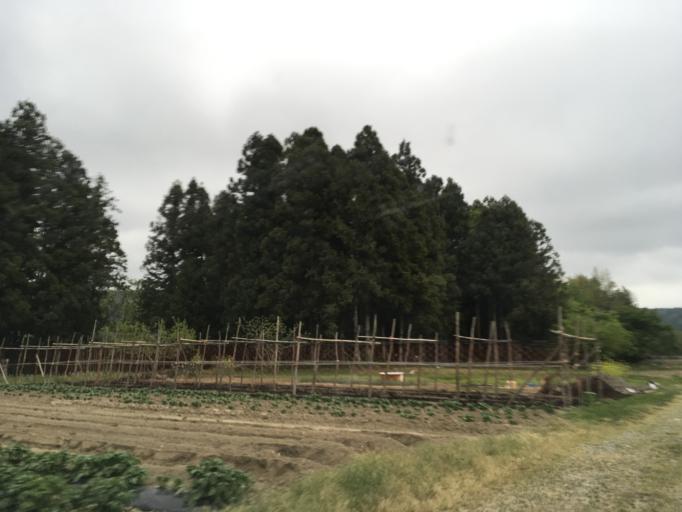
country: JP
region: Miyagi
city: Wakuya
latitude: 38.7188
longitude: 141.2900
